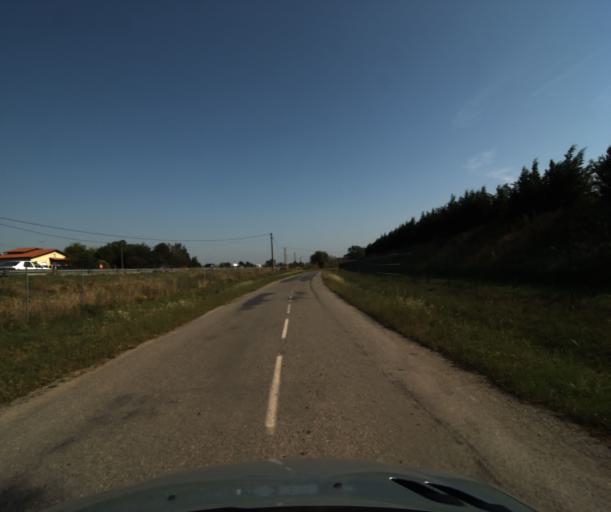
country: FR
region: Midi-Pyrenees
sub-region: Departement de la Haute-Garonne
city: Lacroix-Falgarde
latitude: 43.4789
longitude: 1.4060
